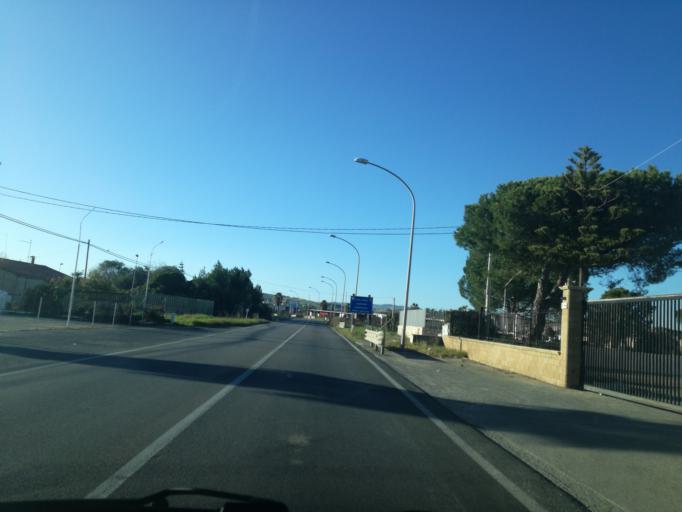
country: IT
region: Sicily
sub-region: Provincia di Caltanissetta
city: Gela
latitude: 37.0959
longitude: 14.1718
